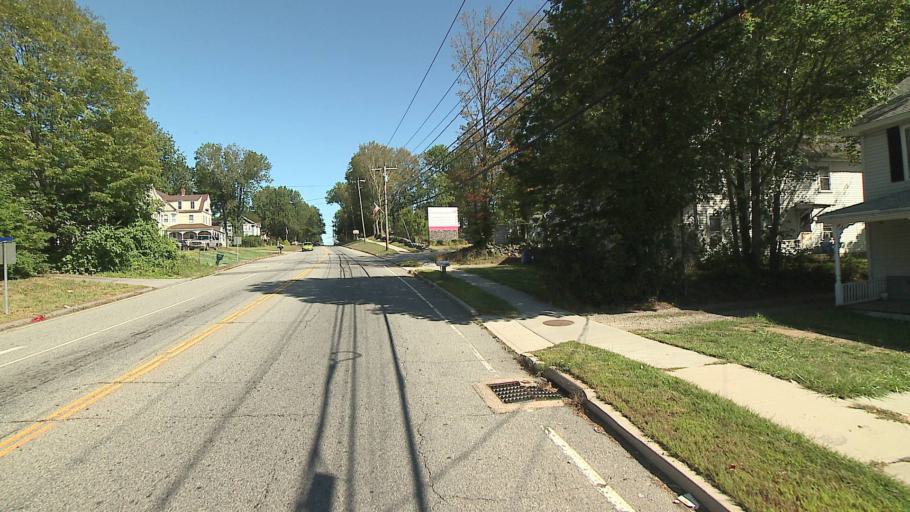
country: US
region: Connecticut
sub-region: Windham County
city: Plainfield
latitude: 41.6805
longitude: -71.9144
